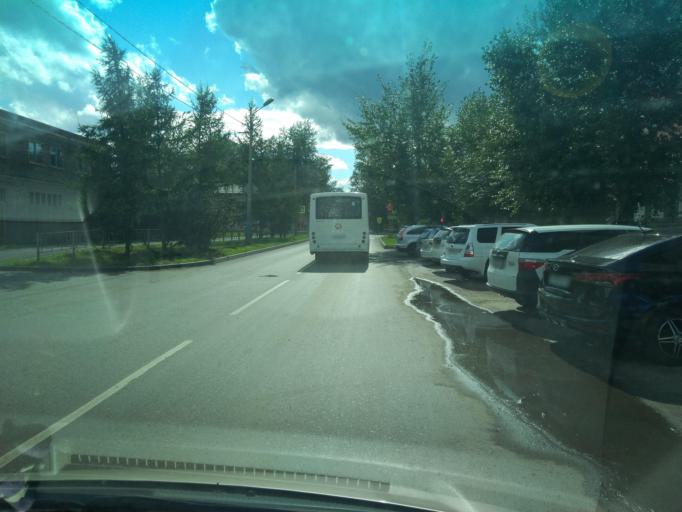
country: RU
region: Krasnoyarskiy
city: Krasnoyarsk
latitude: 55.9924
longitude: 92.9703
